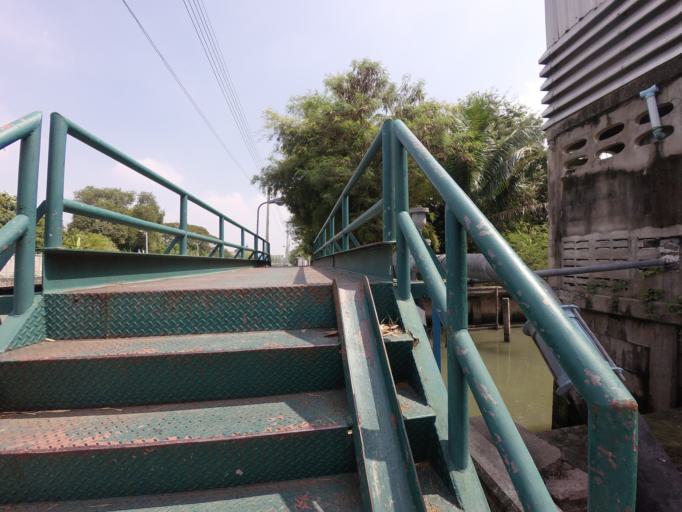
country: TH
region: Bangkok
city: Bueng Kum
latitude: 13.7782
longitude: 100.6700
